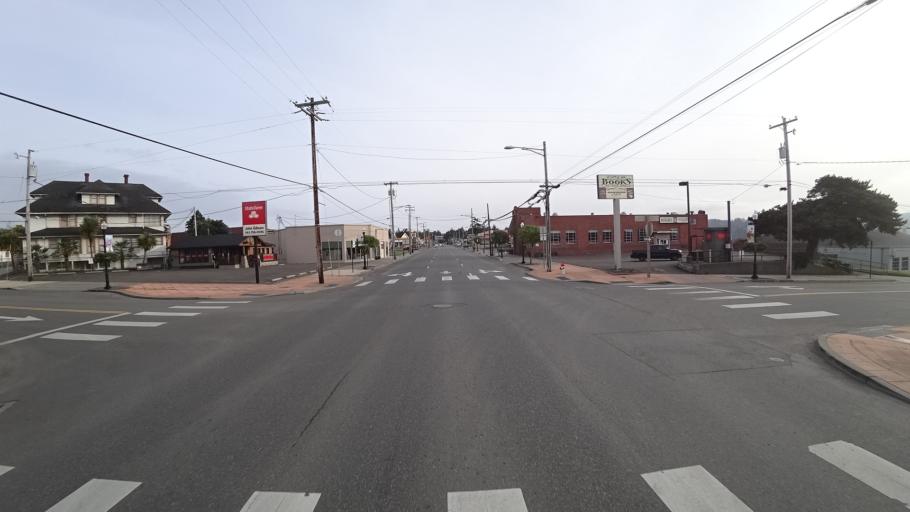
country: US
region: Oregon
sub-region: Coos County
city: North Bend
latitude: 43.4079
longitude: -124.2240
